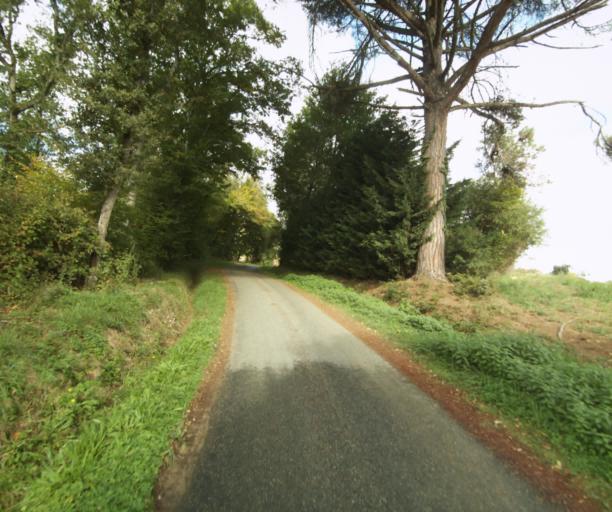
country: FR
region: Midi-Pyrenees
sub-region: Departement du Gers
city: Nogaro
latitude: 43.8363
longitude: -0.0761
